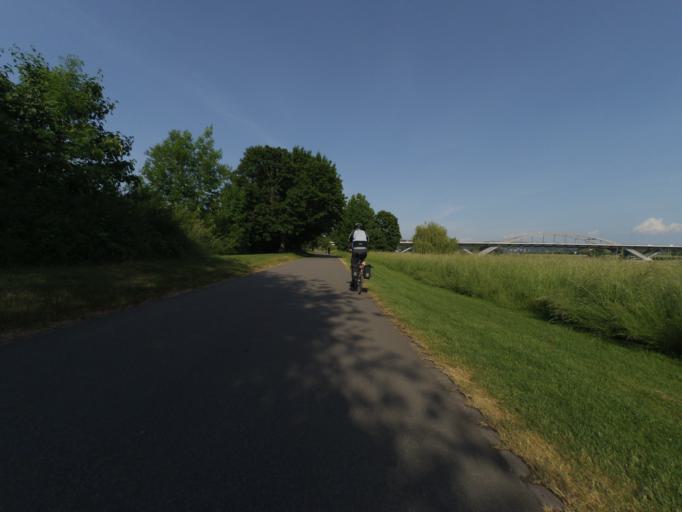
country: DE
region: Saxony
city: Albertstadt
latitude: 51.0654
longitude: 13.7724
